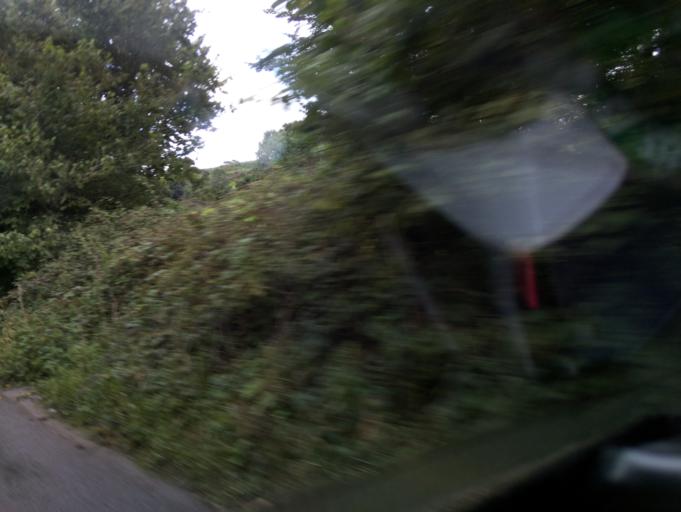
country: GB
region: England
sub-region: Devon
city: Modbury
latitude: 50.3358
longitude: -3.8544
